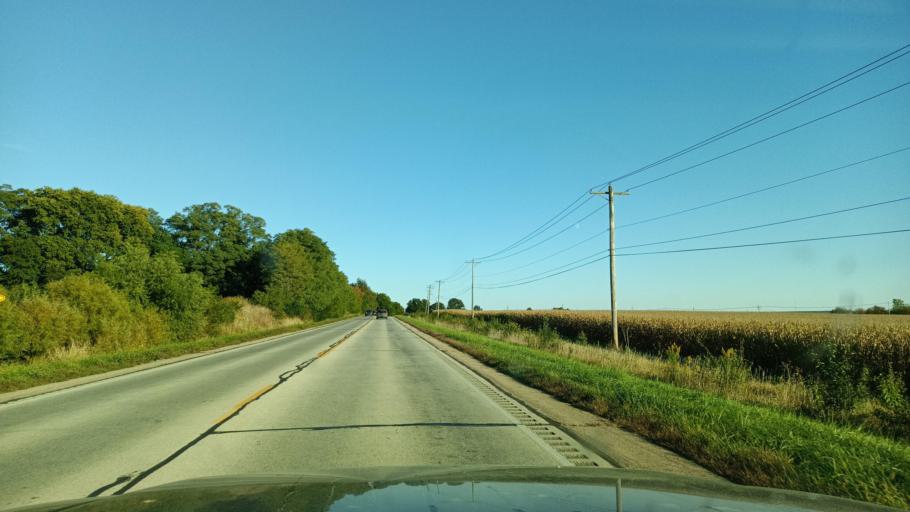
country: US
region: Illinois
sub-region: Champaign County
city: Lake of the Woods
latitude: 40.1638
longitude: -88.3215
